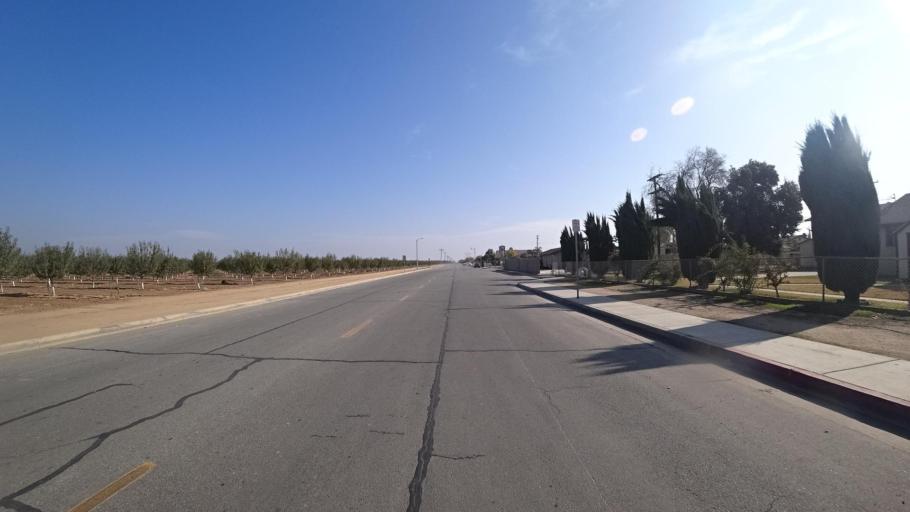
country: US
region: California
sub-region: Kern County
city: McFarland
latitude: 35.6819
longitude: -119.2212
